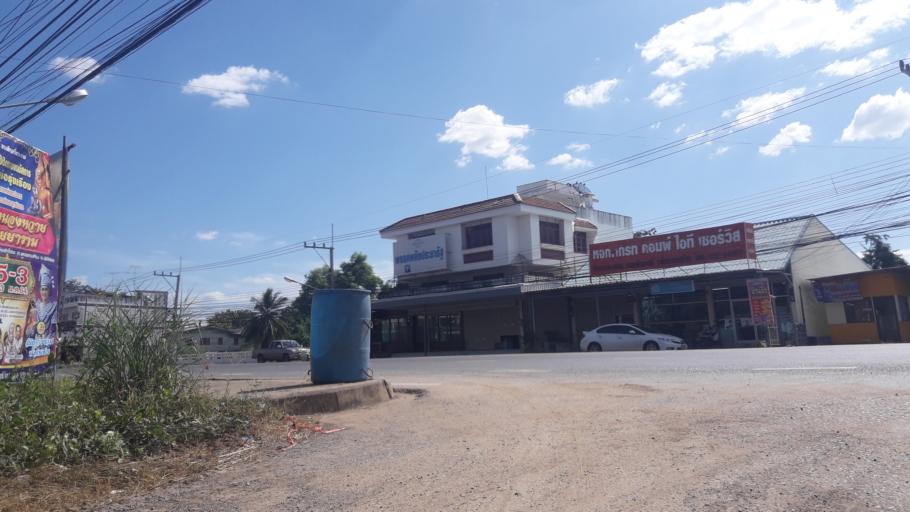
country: TH
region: Phichit
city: Thap Khlo
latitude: 16.1669
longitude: 100.5820
